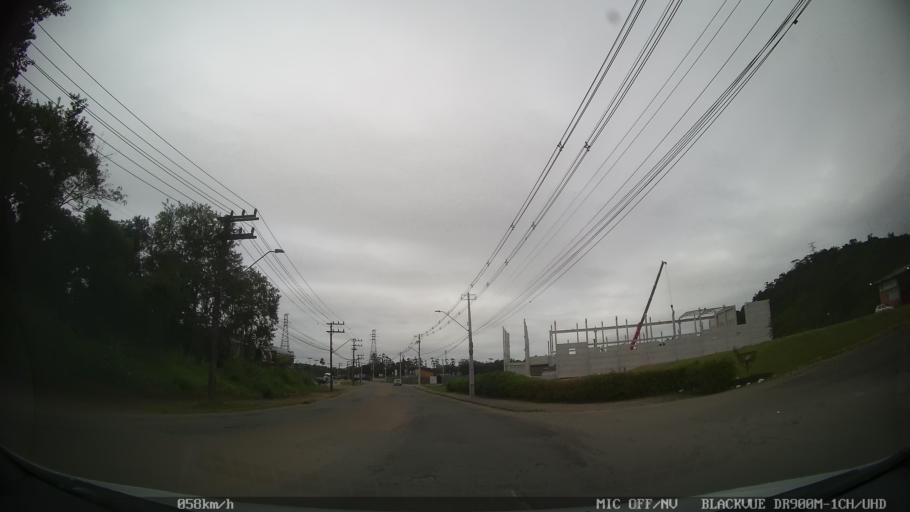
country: BR
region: Santa Catarina
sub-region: Joinville
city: Joinville
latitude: -26.2217
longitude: -48.9052
